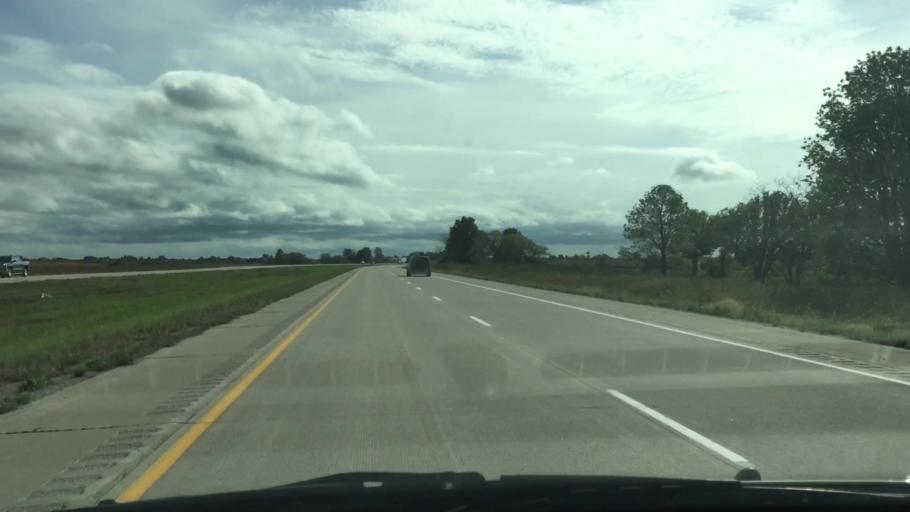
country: US
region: Iowa
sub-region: Decatur County
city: Leon
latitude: 40.8482
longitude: -93.8044
